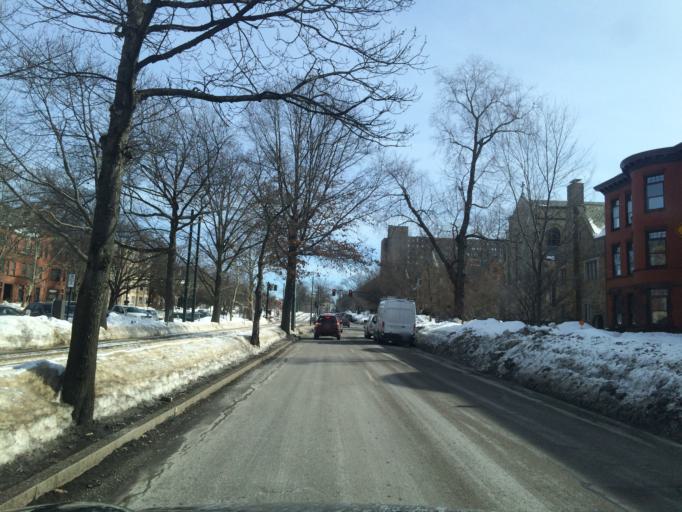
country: US
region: Massachusetts
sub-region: Norfolk County
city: Brookline
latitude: 42.3373
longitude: -71.1433
